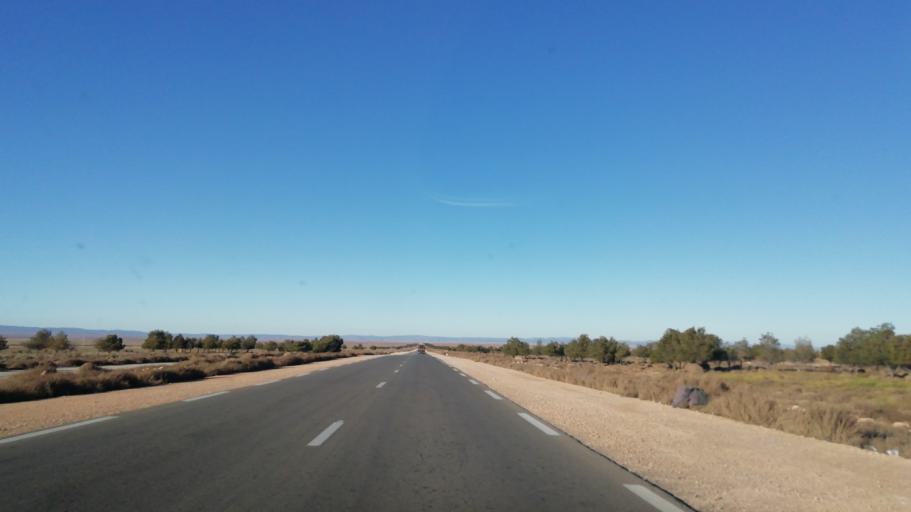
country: DZ
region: Tlemcen
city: Sebdou
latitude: 34.3217
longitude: -1.2633
